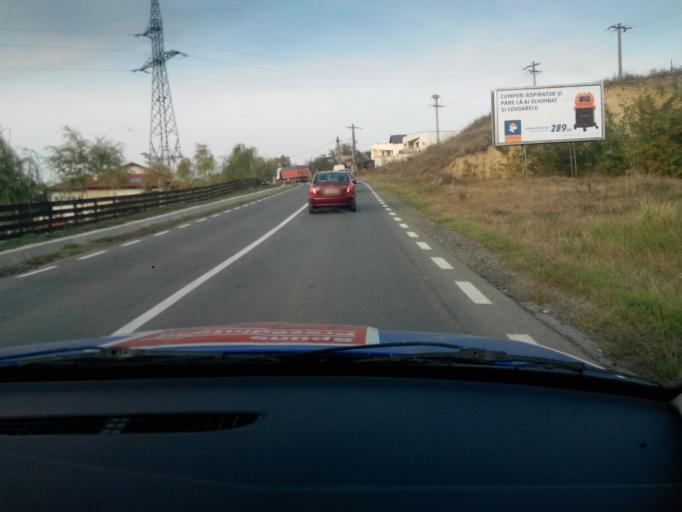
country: RO
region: Tulcea
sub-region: Comuna Somova
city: Mineri
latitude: 45.1669
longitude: 28.7342
